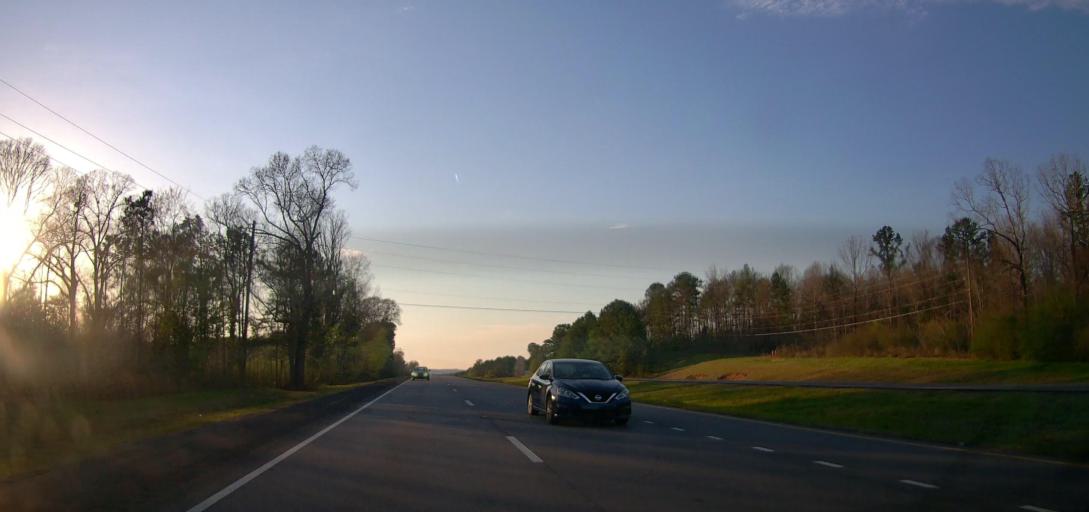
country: US
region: Alabama
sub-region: Talladega County
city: Childersburg
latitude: 33.3121
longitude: -86.3869
